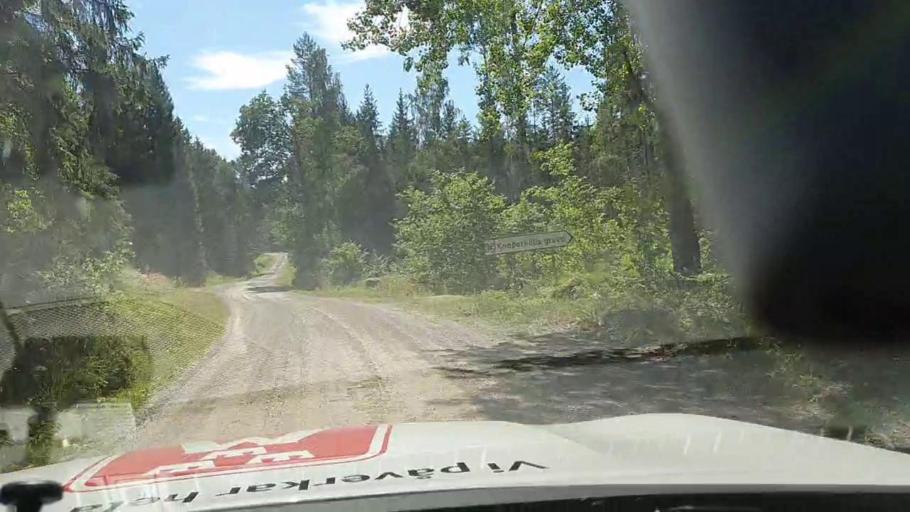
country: SE
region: Soedermanland
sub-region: Strangnas Kommun
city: Akers Styckebruk
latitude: 59.2049
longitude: 16.9174
